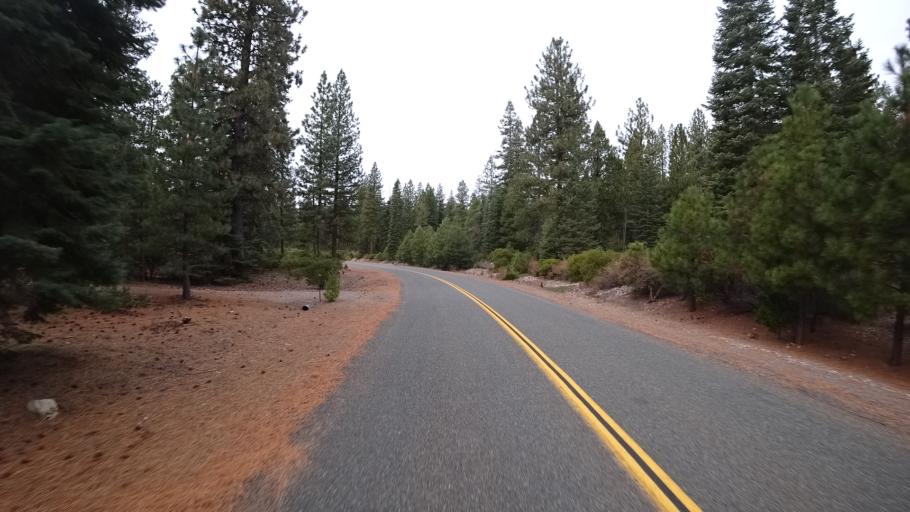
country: US
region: California
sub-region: Siskiyou County
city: Weed
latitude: 41.4133
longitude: -122.3693
